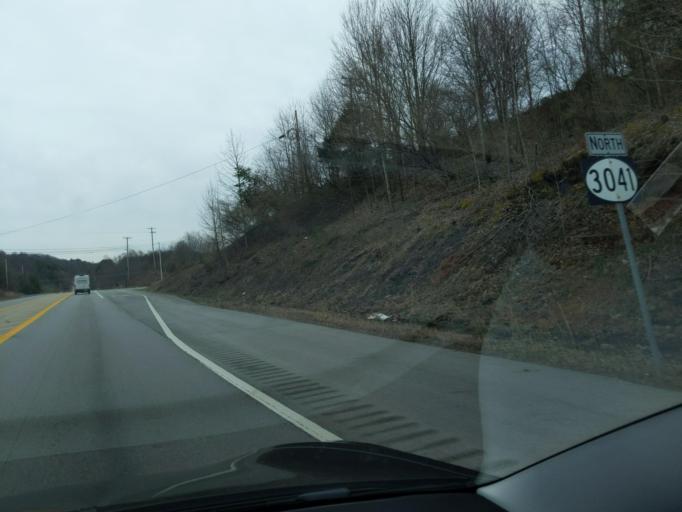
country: US
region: Kentucky
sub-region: Whitley County
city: Corbin
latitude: 36.9167
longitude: -84.0899
